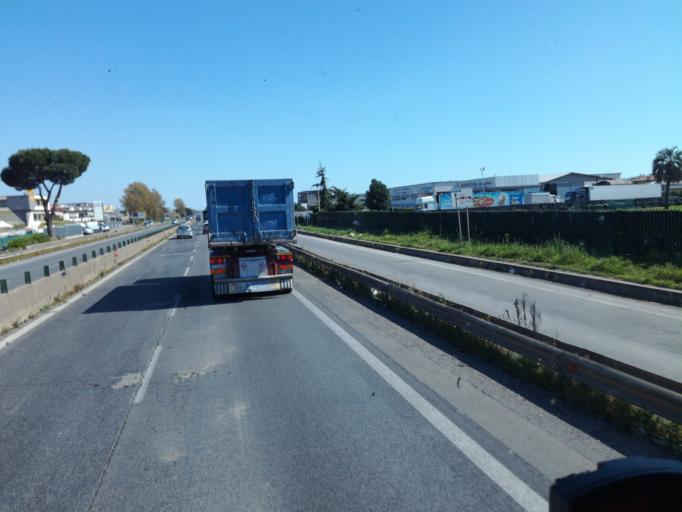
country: IT
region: Latium
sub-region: Provincia di Latina
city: Aprilia
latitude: 41.5764
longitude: 12.6560
